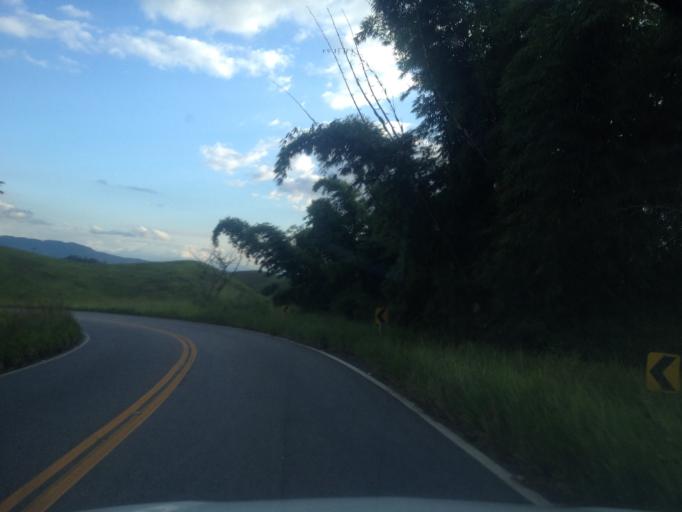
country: BR
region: Rio de Janeiro
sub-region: Quatis
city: Quatis
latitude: -22.3877
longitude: -44.2654
